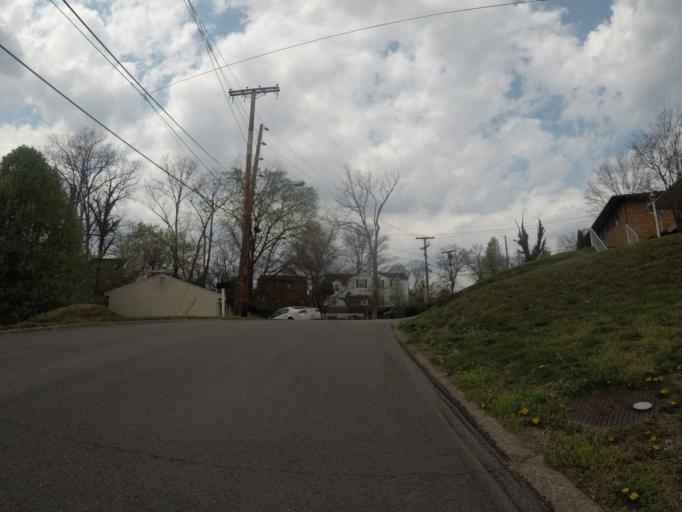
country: US
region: West Virginia
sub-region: Cabell County
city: Huntington
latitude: 38.4080
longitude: -82.3944
